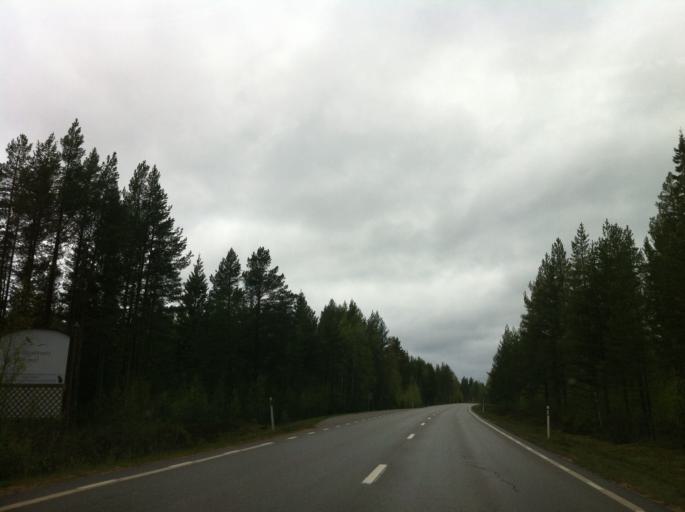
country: SE
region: Jaemtland
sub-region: Harjedalens Kommun
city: Sveg
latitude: 62.0471
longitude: 14.3319
